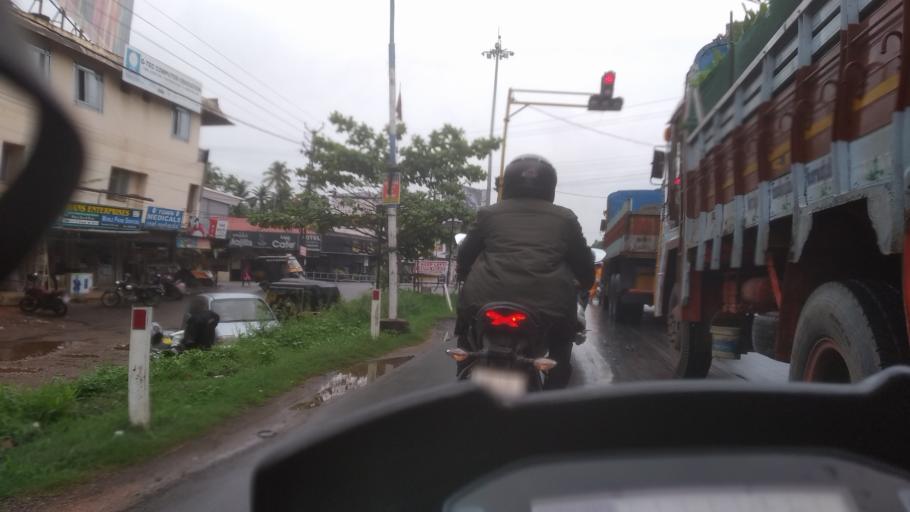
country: IN
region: Kerala
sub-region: Alappuzha
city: Kayankulam
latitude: 9.1758
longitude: 76.4948
